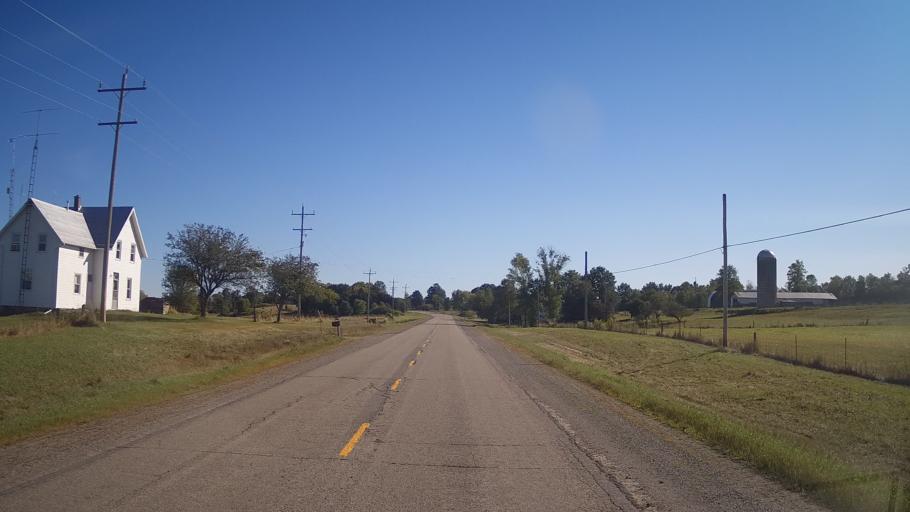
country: CA
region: Ontario
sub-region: Lanark County
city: Smiths Falls
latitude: 44.6122
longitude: -76.0558
